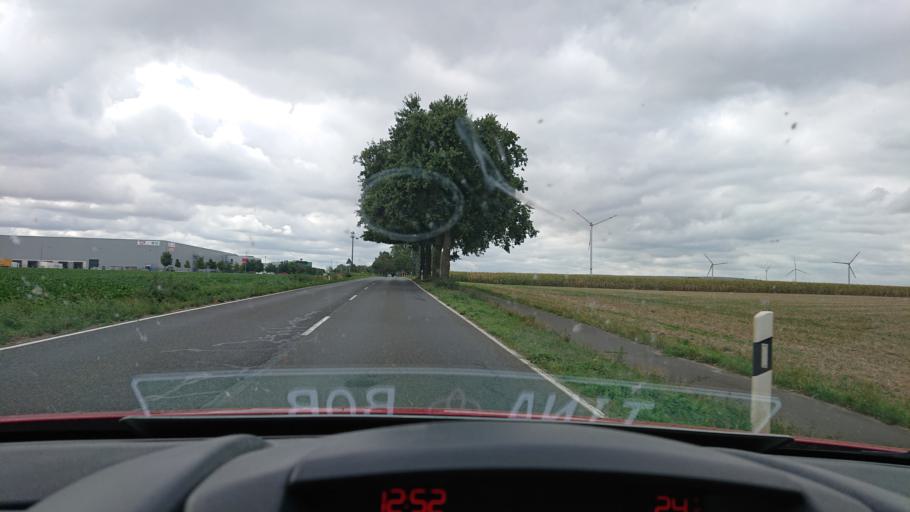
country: DE
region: North Rhine-Westphalia
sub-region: Regierungsbezirk Koln
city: Bedburg
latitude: 50.9636
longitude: 6.5995
